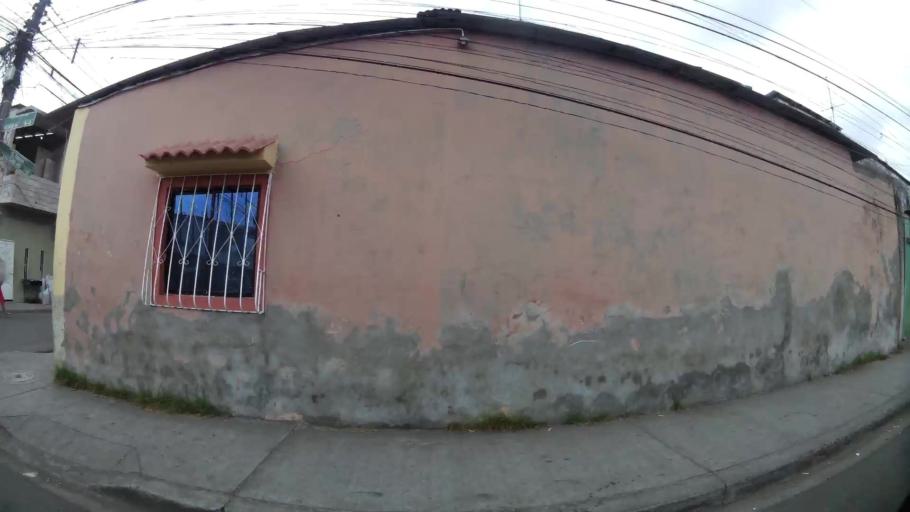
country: EC
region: Guayas
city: Guayaquil
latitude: -2.2343
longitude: -79.9101
